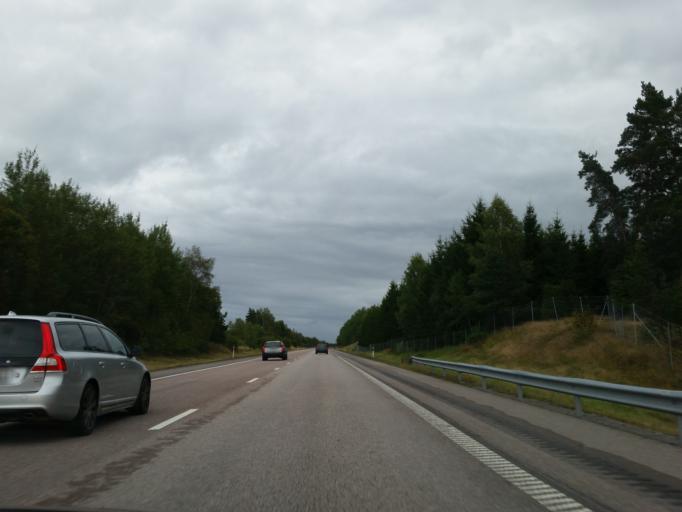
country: SE
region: Uppsala
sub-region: Enkopings Kommun
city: Grillby
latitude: 59.6324
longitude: 17.3032
